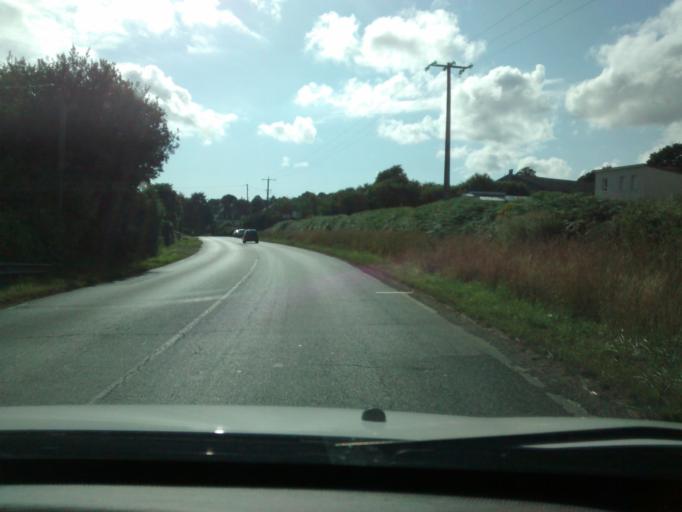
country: FR
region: Brittany
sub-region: Departement des Cotes-d'Armor
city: Rospez
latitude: 48.7410
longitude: -3.4243
